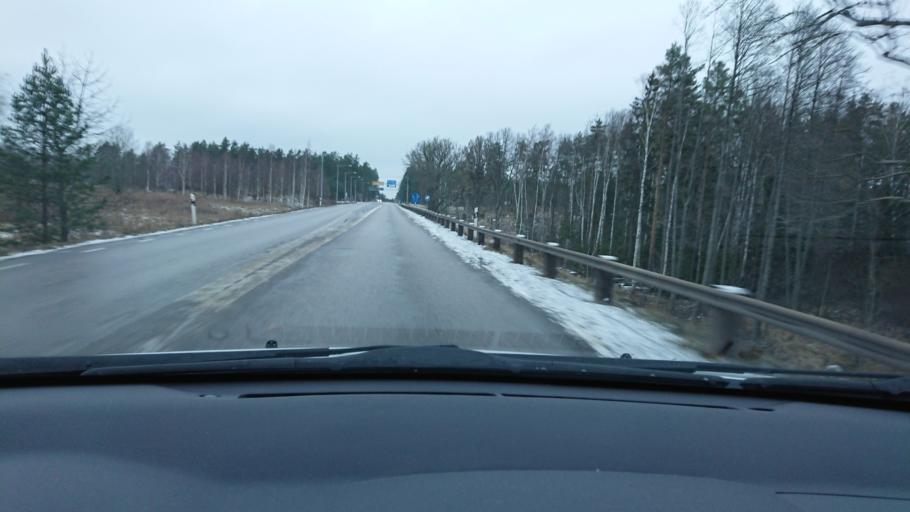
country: SE
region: Kalmar
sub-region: Hultsfreds Kommun
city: Hultsfred
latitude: 57.4868
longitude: 15.8283
